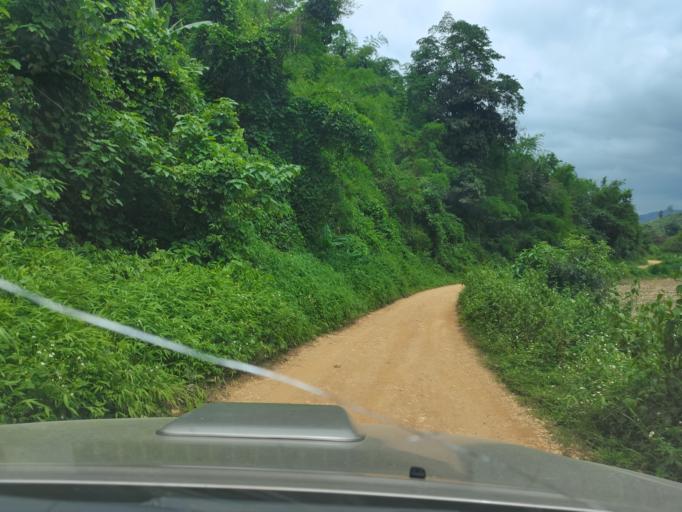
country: TH
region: Phayao
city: Phu Sang
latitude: 19.7262
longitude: 100.4836
